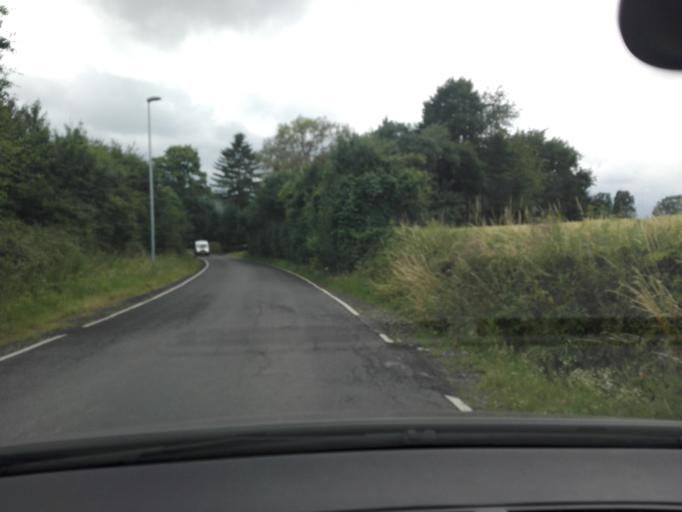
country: DE
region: North Rhine-Westphalia
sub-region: Regierungsbezirk Arnsberg
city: Unna
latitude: 51.5133
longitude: 7.6670
